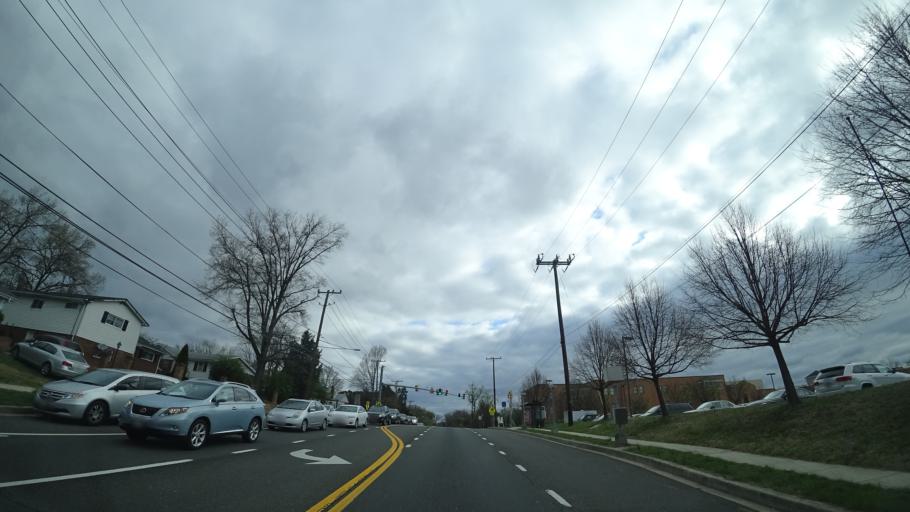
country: US
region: Maryland
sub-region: Montgomery County
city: Takoma Park
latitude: 38.9848
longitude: -77.0147
